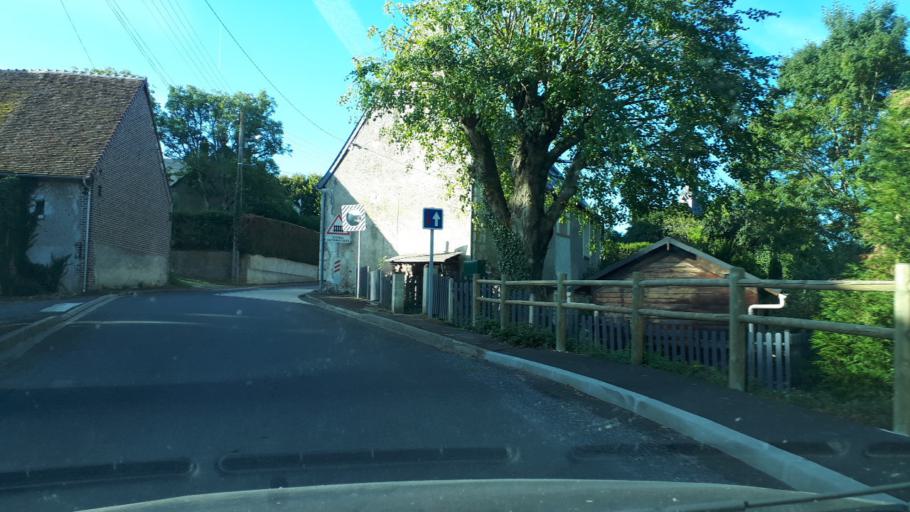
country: FR
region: Centre
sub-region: Departement d'Indre-et-Loire
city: Chateau-Renault
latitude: 47.6504
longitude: 0.9421
